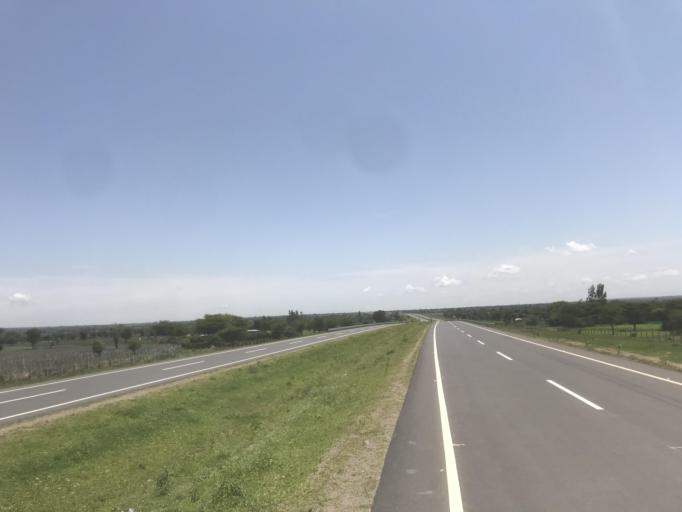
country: ET
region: Oromiya
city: Mojo
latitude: 8.3462
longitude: 38.9781
